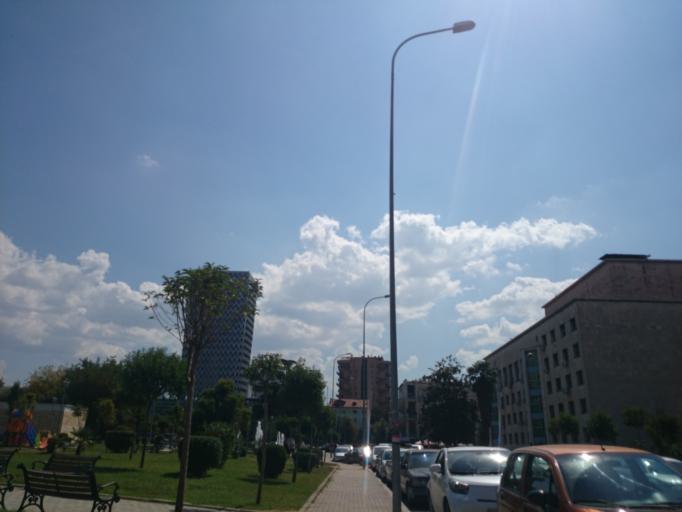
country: AL
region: Tirane
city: Tirana
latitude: 41.3299
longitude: 19.8200
